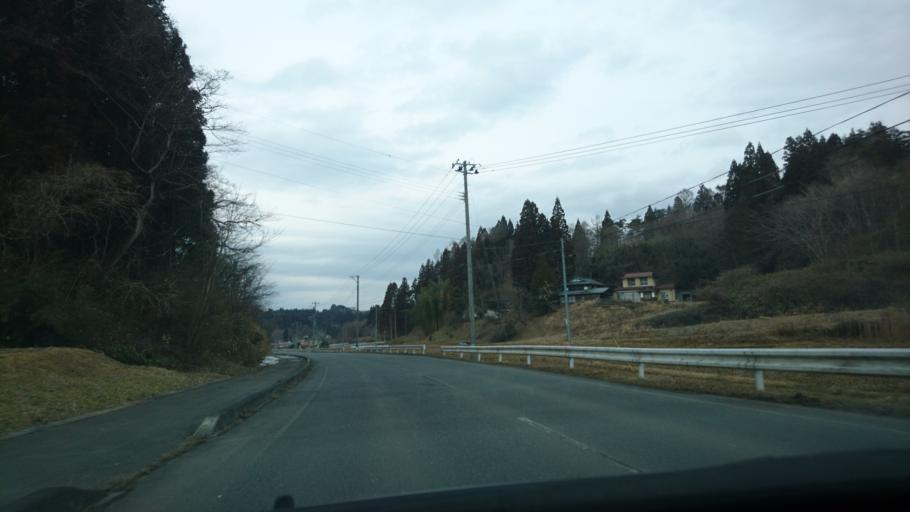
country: JP
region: Iwate
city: Ichinoseki
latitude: 38.9489
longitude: 141.3631
